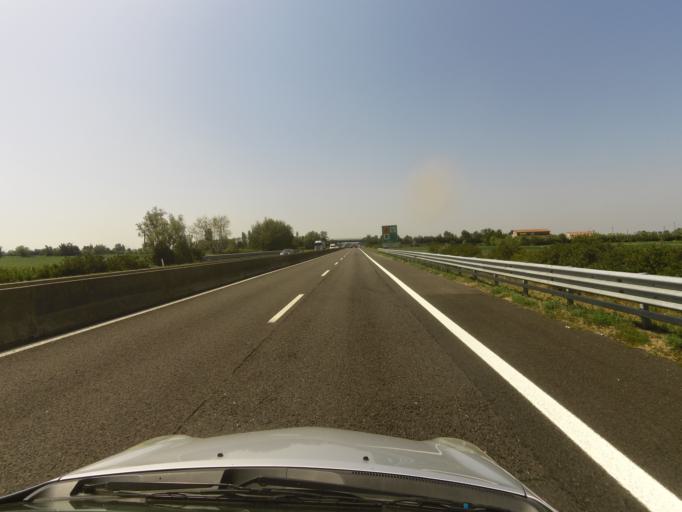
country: IT
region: Veneto
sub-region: Provincia di Rovigo
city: Costa di Rovigo
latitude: 45.0470
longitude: 11.7143
